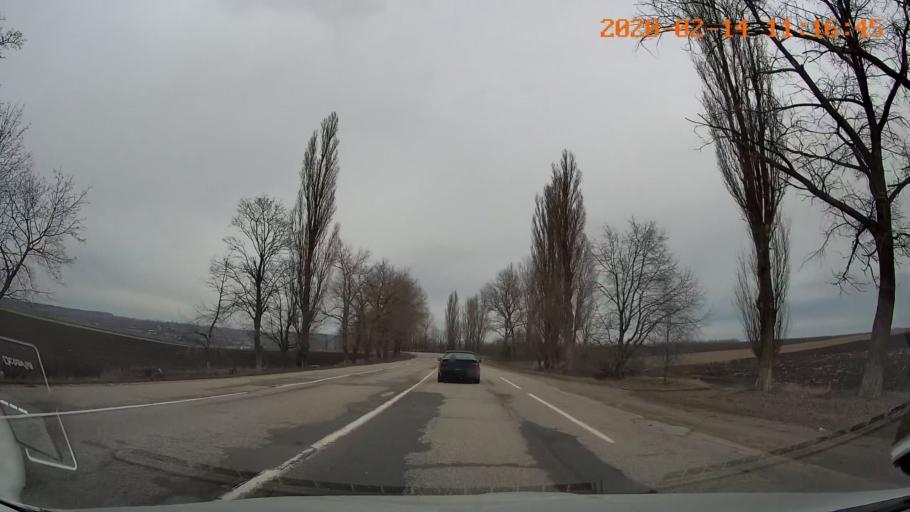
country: MD
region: Raionul Edinet
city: Edinet
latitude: 48.2544
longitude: 27.2005
